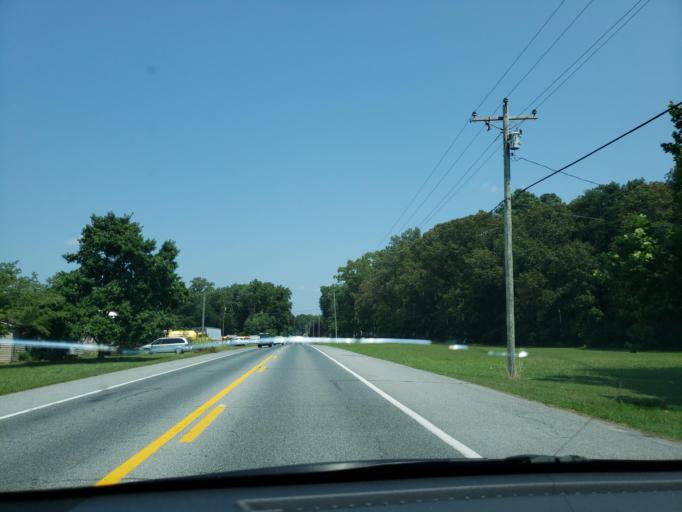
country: US
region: Delaware
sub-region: Sussex County
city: Milton
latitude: 38.8167
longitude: -75.3087
